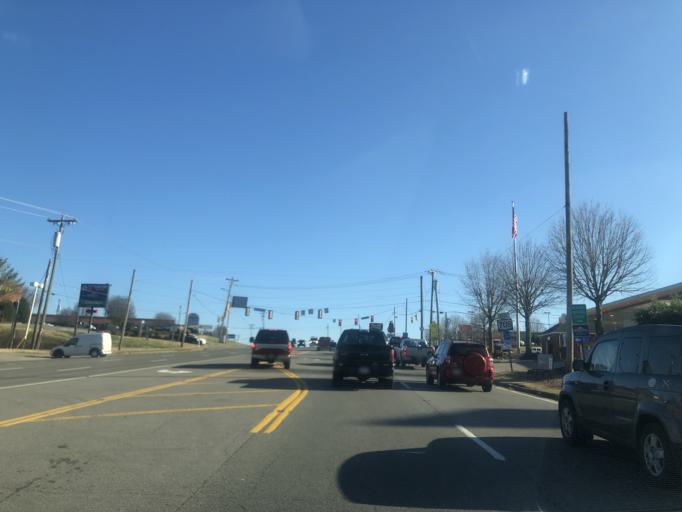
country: US
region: Tennessee
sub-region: Cheatham County
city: Pegram
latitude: 36.0802
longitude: -86.9546
